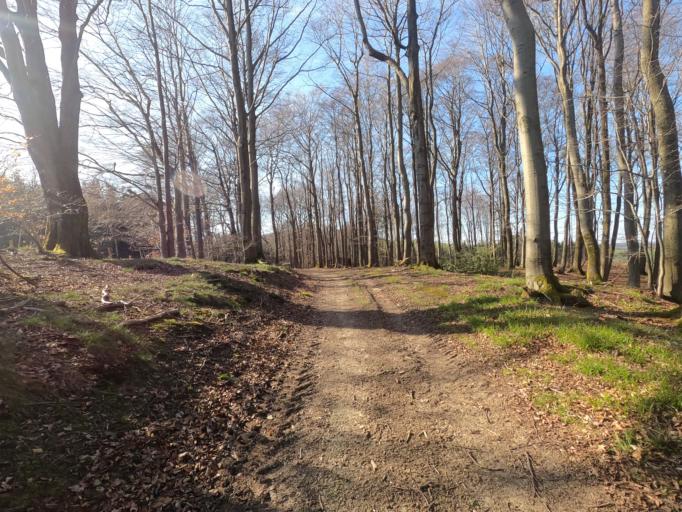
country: DE
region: North Rhine-Westphalia
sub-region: Regierungsbezirk Arnsberg
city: Herscheid
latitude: 51.1714
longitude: 7.7126
